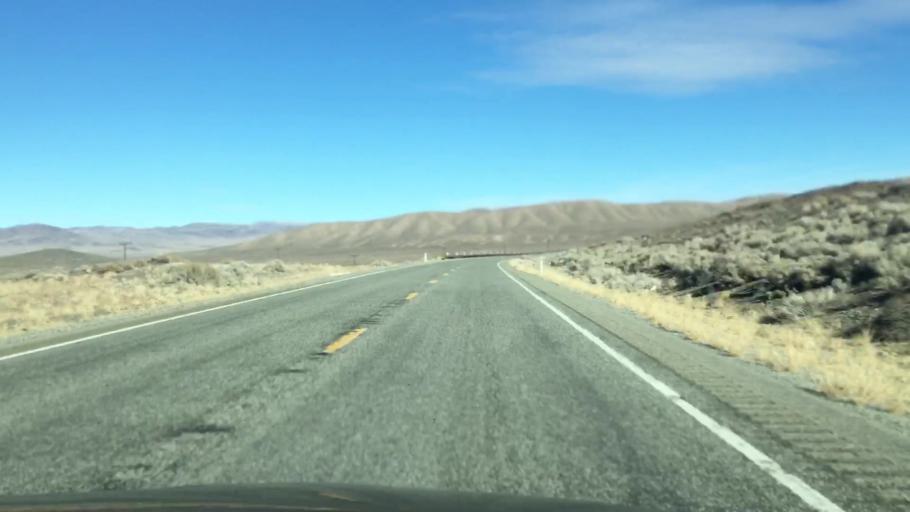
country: US
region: Nevada
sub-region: Lyon County
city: Yerington
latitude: 39.0425
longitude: -118.9829
